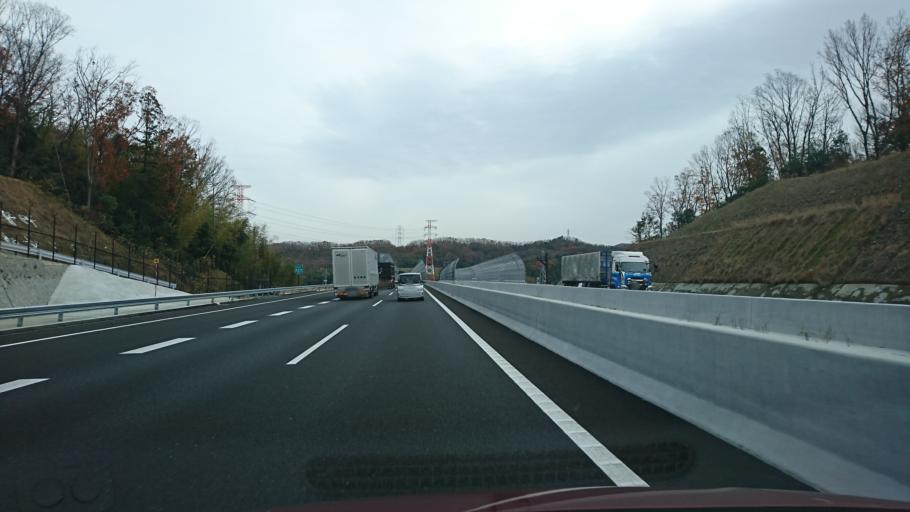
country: JP
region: Hyogo
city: Sandacho
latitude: 34.8519
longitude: 135.2320
